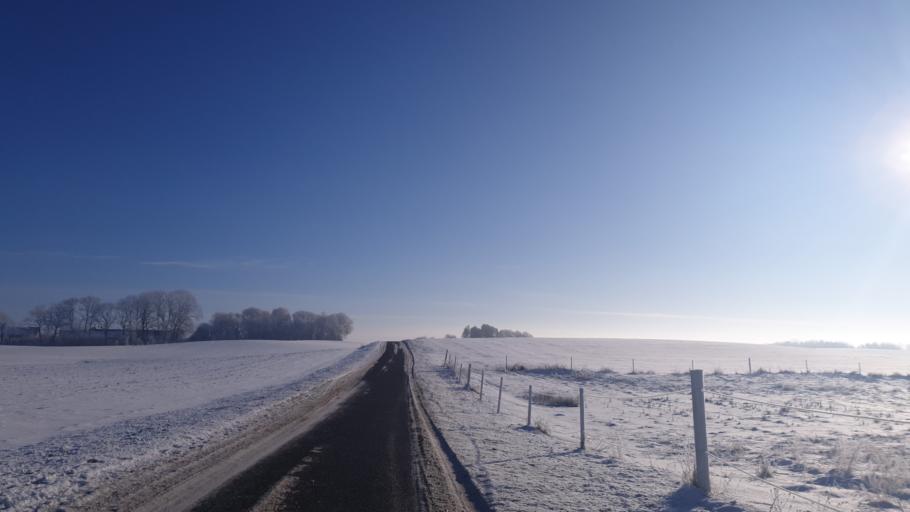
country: DK
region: Central Jutland
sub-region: Hedensted Kommune
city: Hedensted
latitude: 55.8047
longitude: 9.7367
